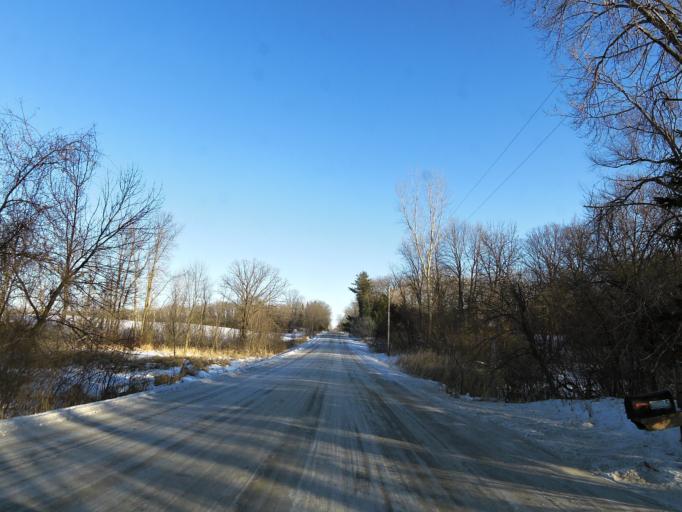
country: US
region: Minnesota
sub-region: Hennepin County
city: Mound
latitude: 44.9567
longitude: -93.6821
